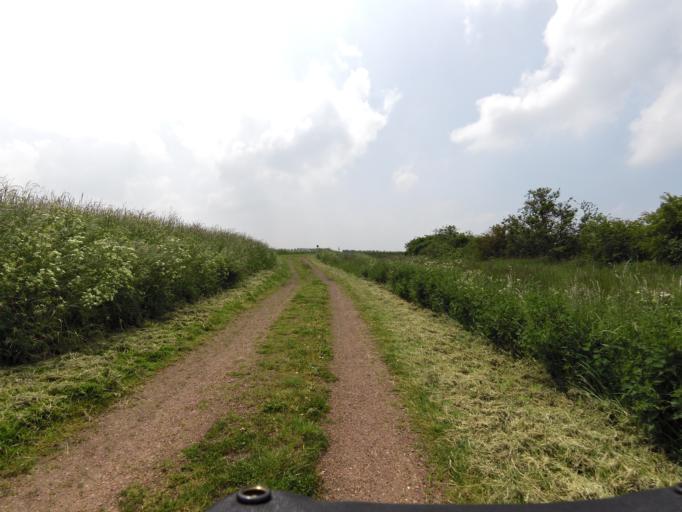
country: NL
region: South Holland
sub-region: Gemeente Spijkenisse
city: Spijkenisse
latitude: 51.8166
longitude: 4.2825
